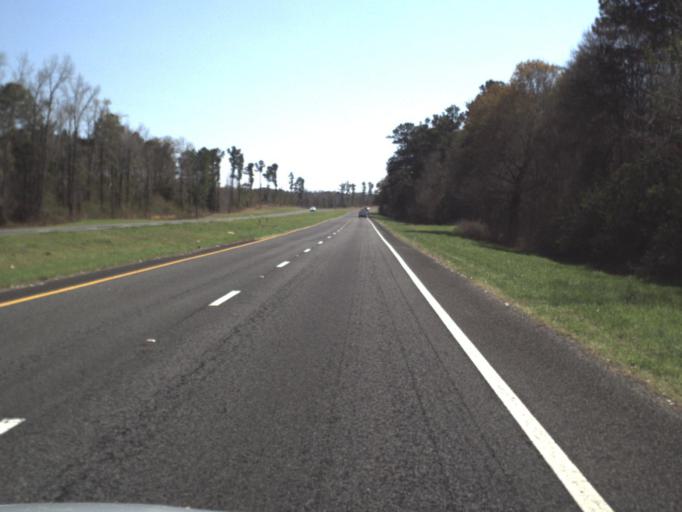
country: US
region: Florida
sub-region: Jackson County
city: Graceville
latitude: 30.9653
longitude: -85.4070
